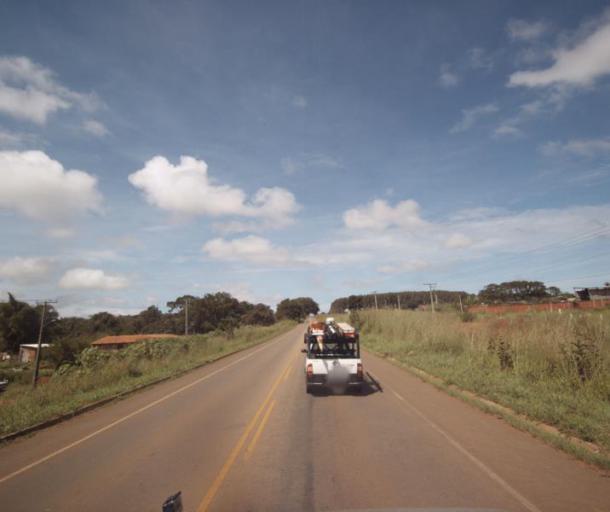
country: BR
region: Goias
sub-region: Anapolis
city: Anapolis
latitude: -16.2733
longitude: -48.9406
